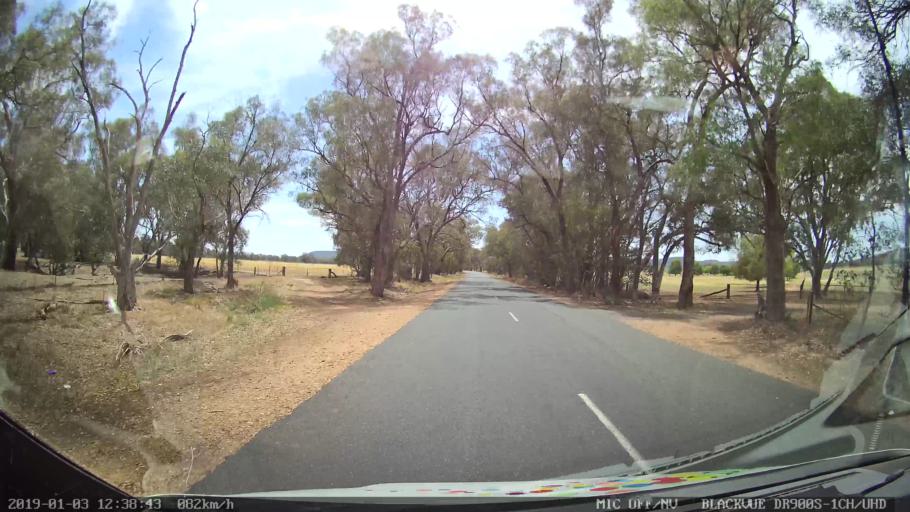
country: AU
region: New South Wales
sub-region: Weddin
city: Grenfell
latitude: -33.8312
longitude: 148.1990
